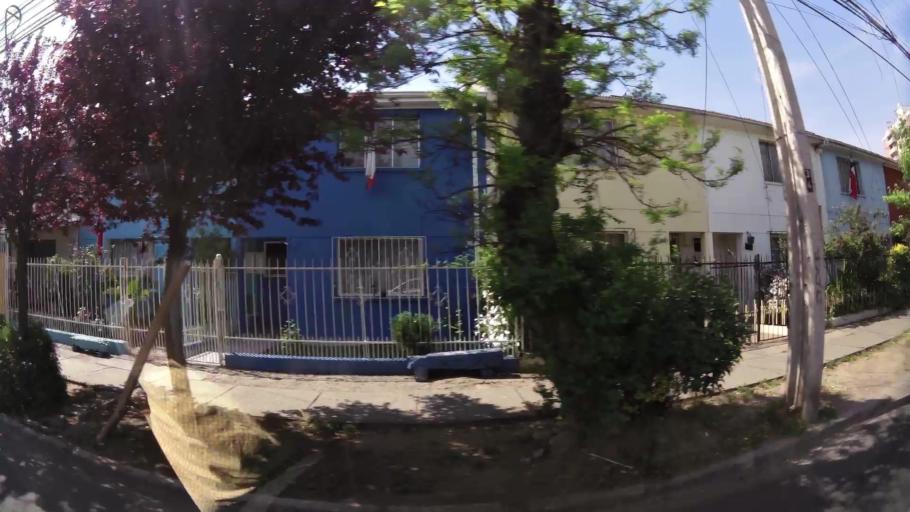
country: CL
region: Santiago Metropolitan
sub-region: Provincia de Santiago
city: Lo Prado
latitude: -33.4197
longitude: -70.7029
